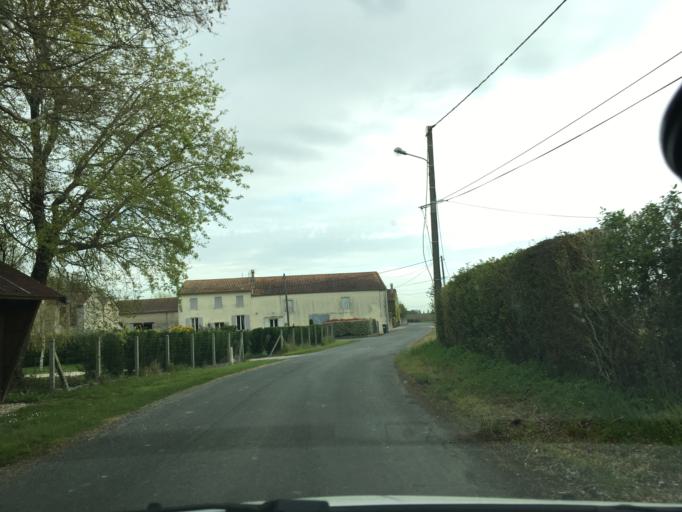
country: FR
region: Aquitaine
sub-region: Departement de la Gironde
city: Lesparre-Medoc
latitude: 45.3114
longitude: -0.8932
